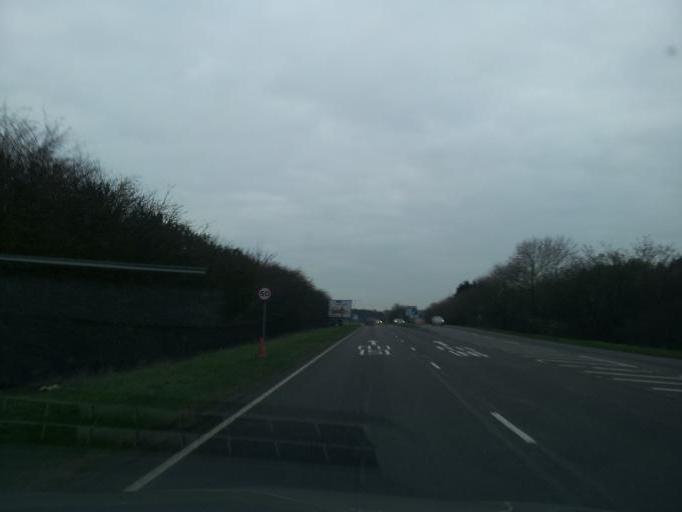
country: GB
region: England
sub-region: Cambridgeshire
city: Grantchester
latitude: 52.1938
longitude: 0.0817
